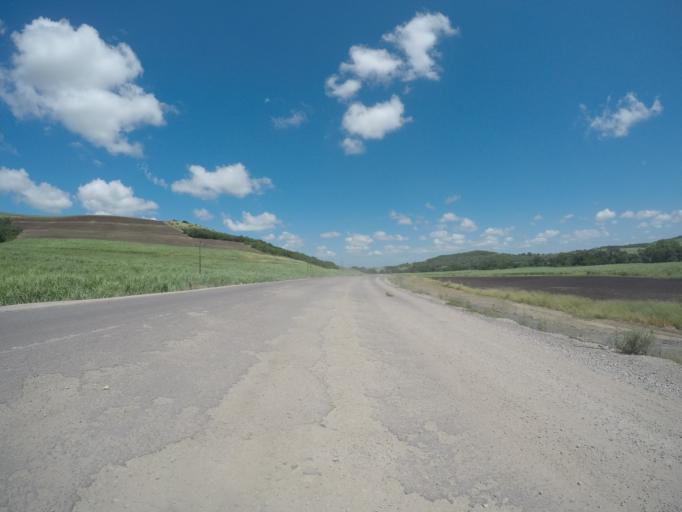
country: ZA
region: KwaZulu-Natal
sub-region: uThungulu District Municipality
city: Empangeni
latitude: -28.6502
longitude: 31.7689
